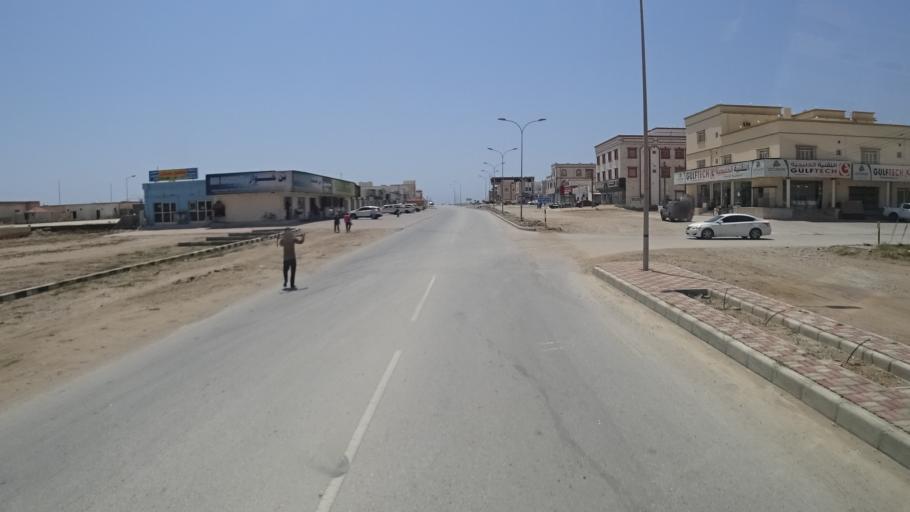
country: OM
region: Zufar
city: Salalah
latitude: 16.9838
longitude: 54.6937
